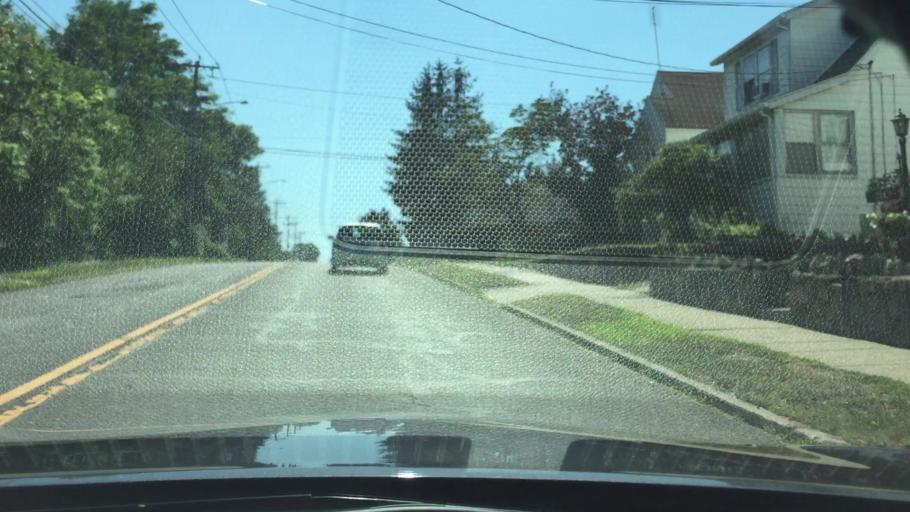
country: US
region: Connecticut
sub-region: Fairfield County
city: Trumbull
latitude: 41.2076
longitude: -73.1968
